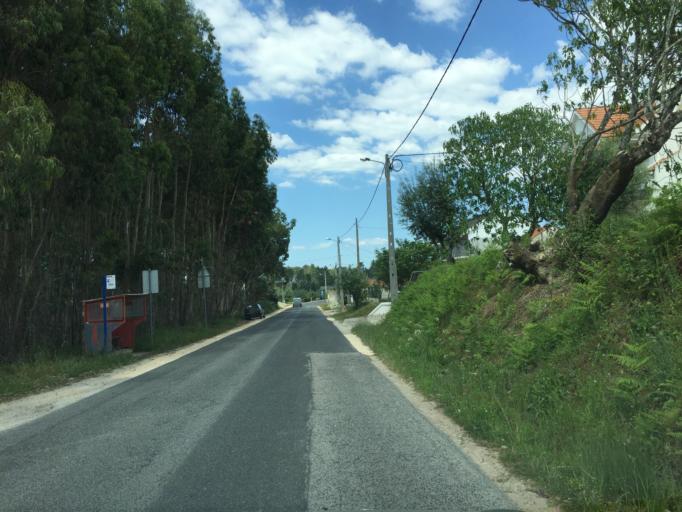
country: PT
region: Santarem
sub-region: Ourem
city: Ourem
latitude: 39.6892
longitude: -8.5452
